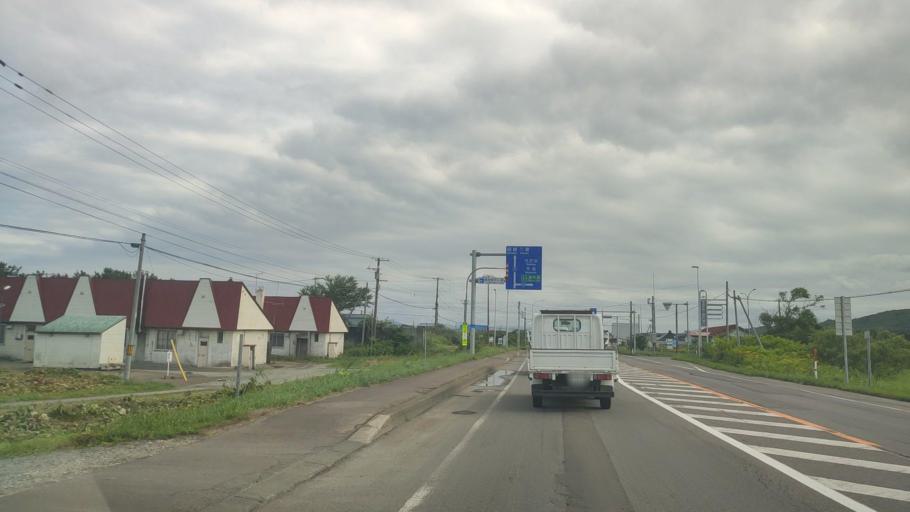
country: JP
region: Hokkaido
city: Niseko Town
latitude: 42.4415
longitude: 140.3258
